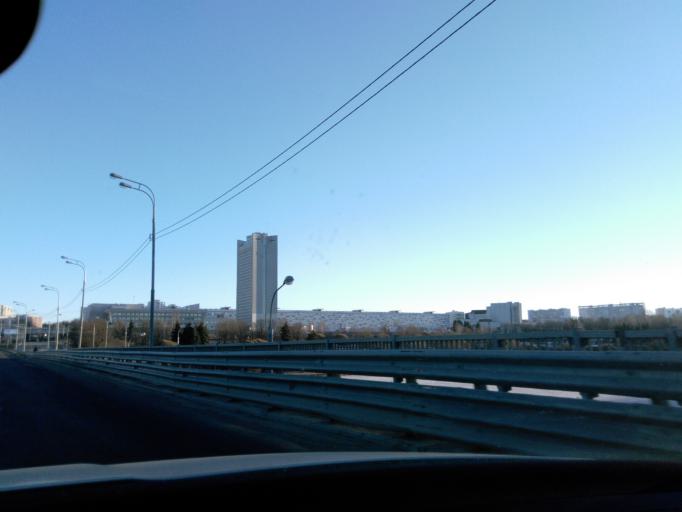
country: RU
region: Moscow
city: Zelenograd
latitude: 55.9866
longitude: 37.2124
